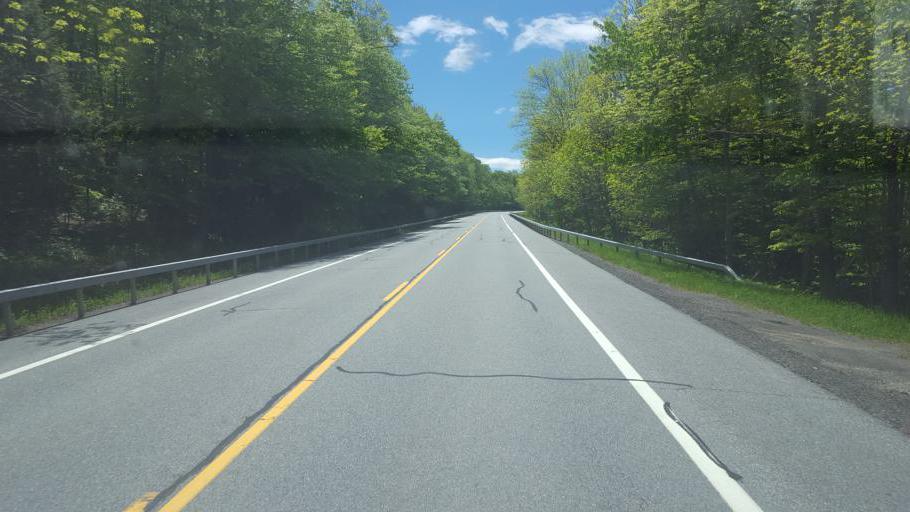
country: US
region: New York
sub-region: Hamilton County
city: Lake Pleasant
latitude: 43.6239
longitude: -74.4067
